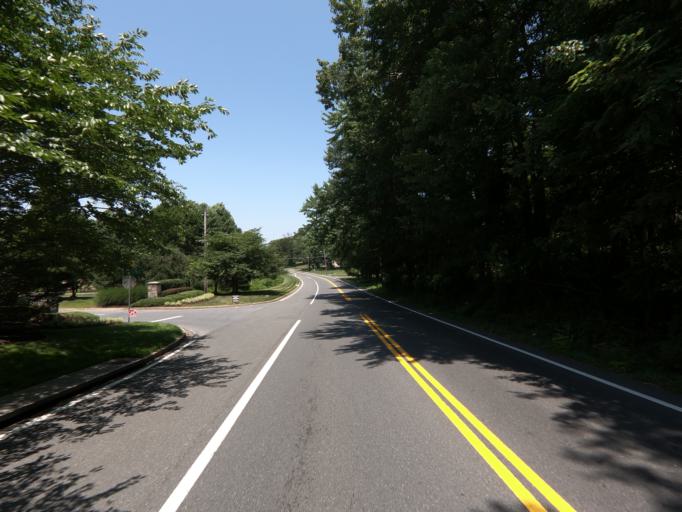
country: US
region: Maryland
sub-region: Montgomery County
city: Clarksburg
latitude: 39.2666
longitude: -77.3057
